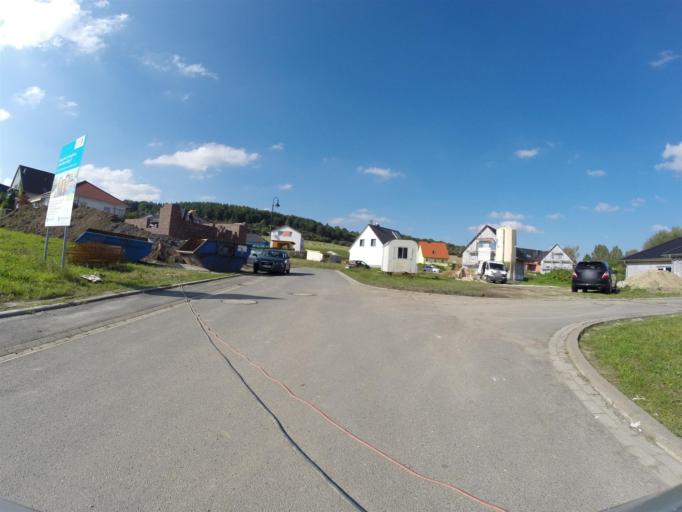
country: DE
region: Thuringia
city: Schongleina
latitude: 50.9082
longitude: 11.7222
